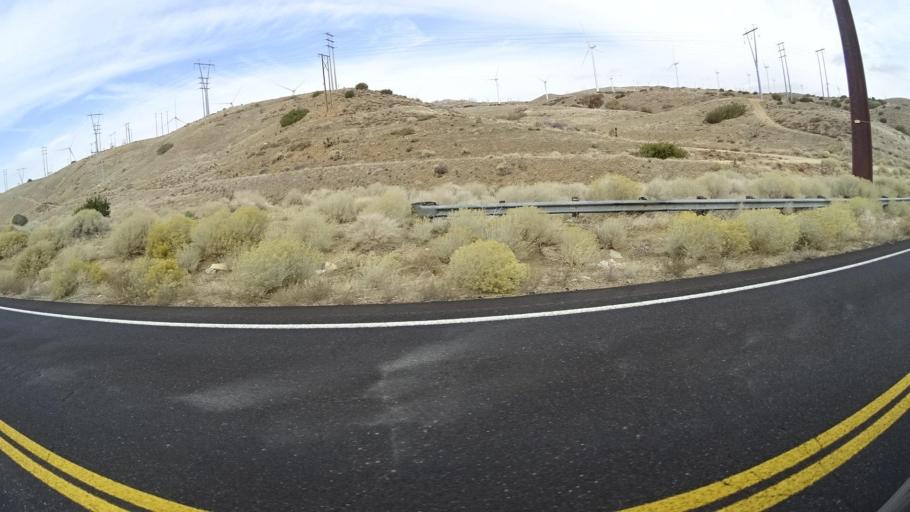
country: US
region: California
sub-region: Kern County
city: Tehachapi
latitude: 35.0517
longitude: -118.3430
